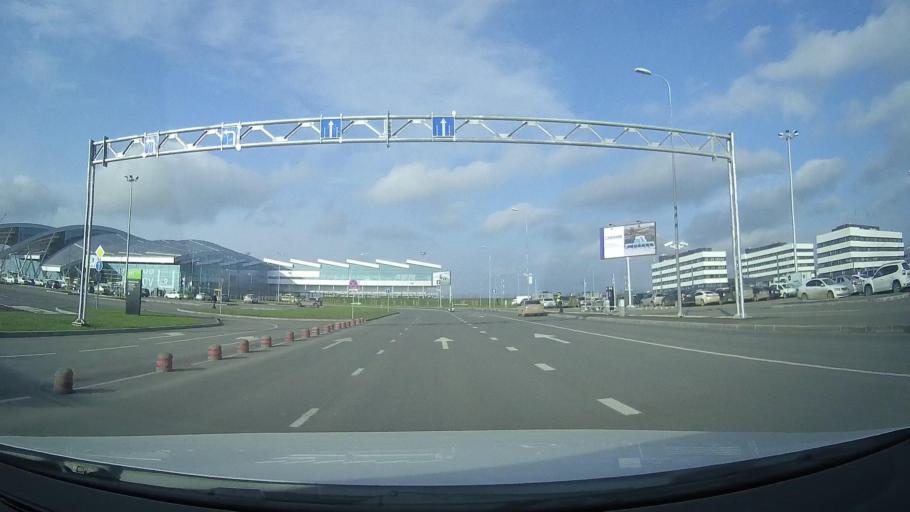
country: RU
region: Rostov
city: Grushevskaya
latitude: 47.4878
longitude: 39.9324
